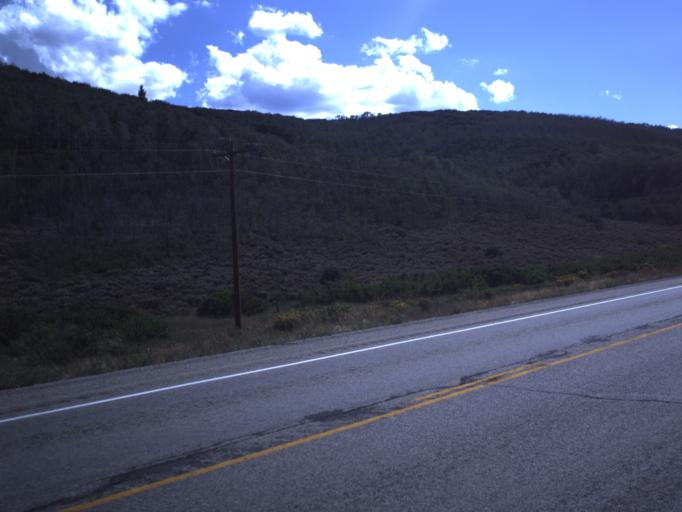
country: US
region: Utah
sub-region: Summit County
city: Francis
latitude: 40.2021
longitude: -110.9856
